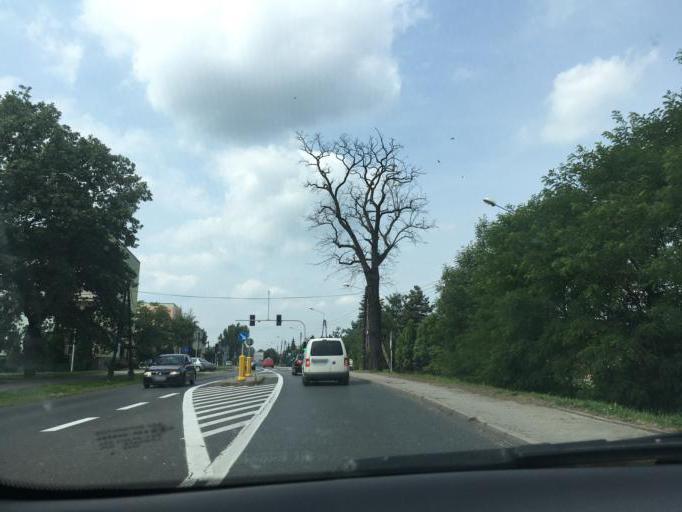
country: PL
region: Lesser Poland Voivodeship
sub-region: Powiat oswiecimski
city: Babice
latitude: 50.0785
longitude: 19.1732
